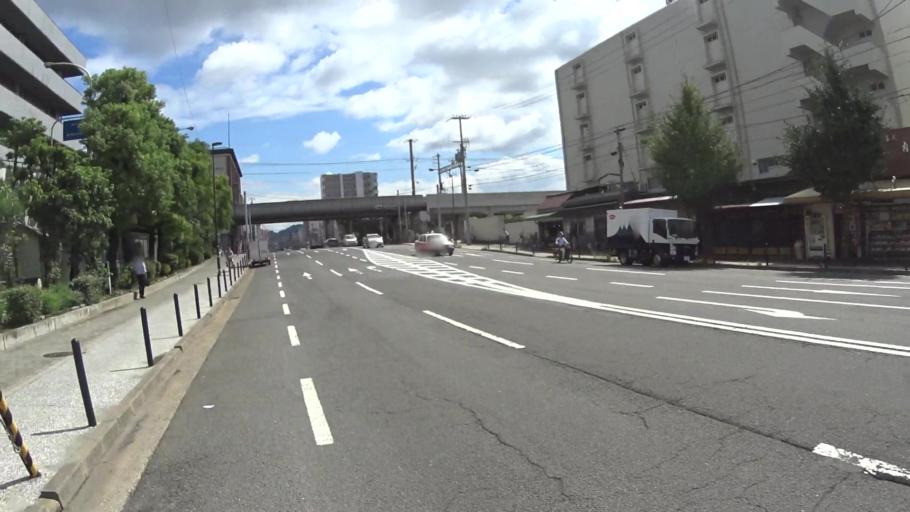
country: JP
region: Kyoto
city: Kyoto
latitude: 34.9894
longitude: 135.7423
